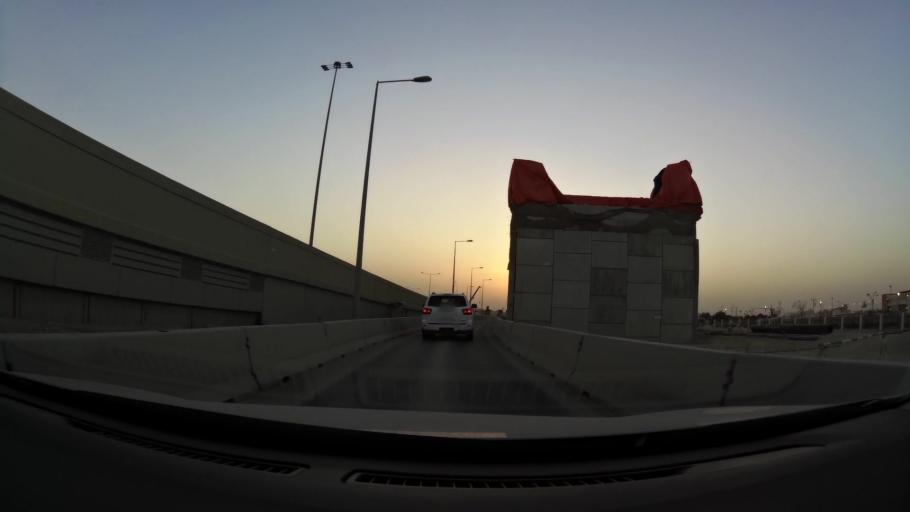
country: QA
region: Baladiyat ar Rayyan
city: Ar Rayyan
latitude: 25.2953
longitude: 51.4715
